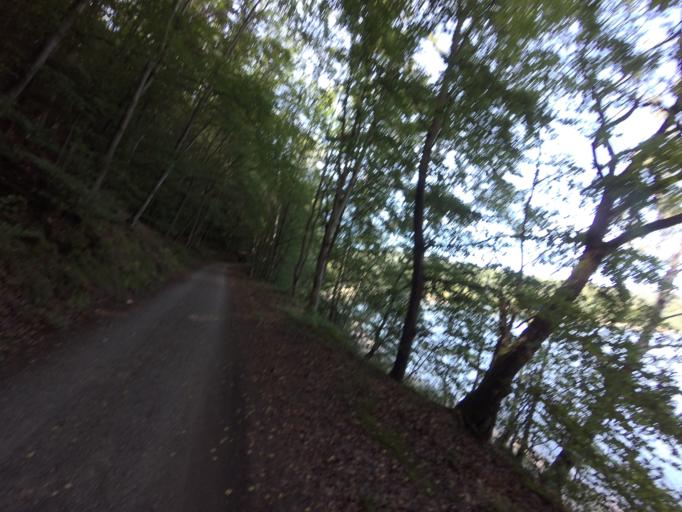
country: DE
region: North Rhine-Westphalia
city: Heimbach
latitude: 50.6354
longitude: 6.4062
